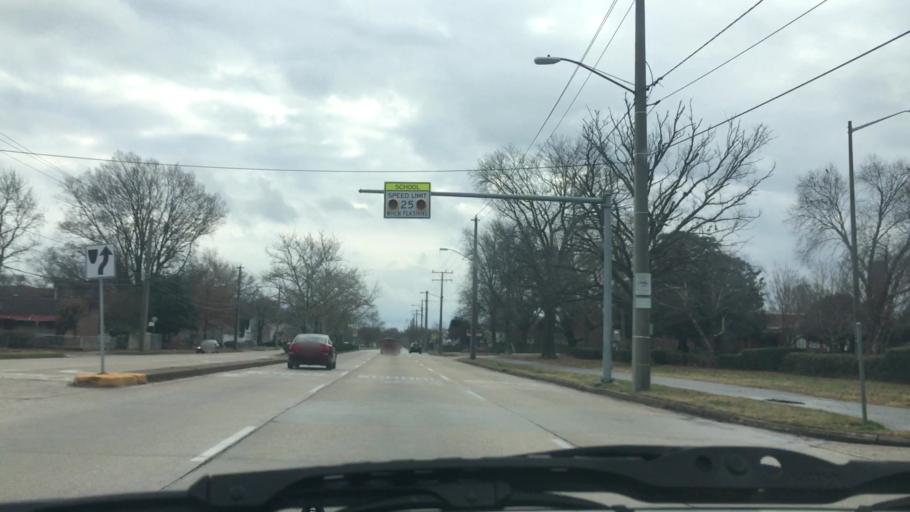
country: US
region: Virginia
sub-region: City of Norfolk
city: Norfolk
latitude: 36.8982
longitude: -76.2389
